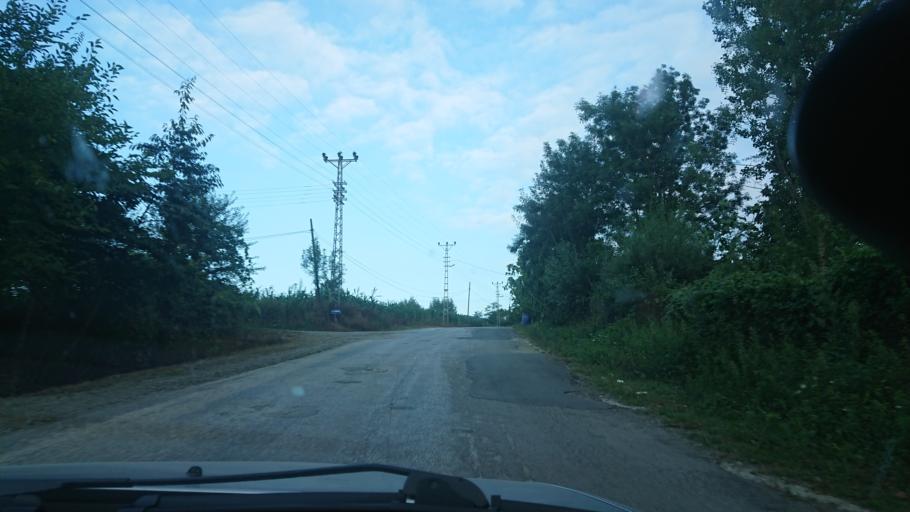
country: TR
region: Samsun
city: Tekkekoy
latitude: 41.1728
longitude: 36.5300
